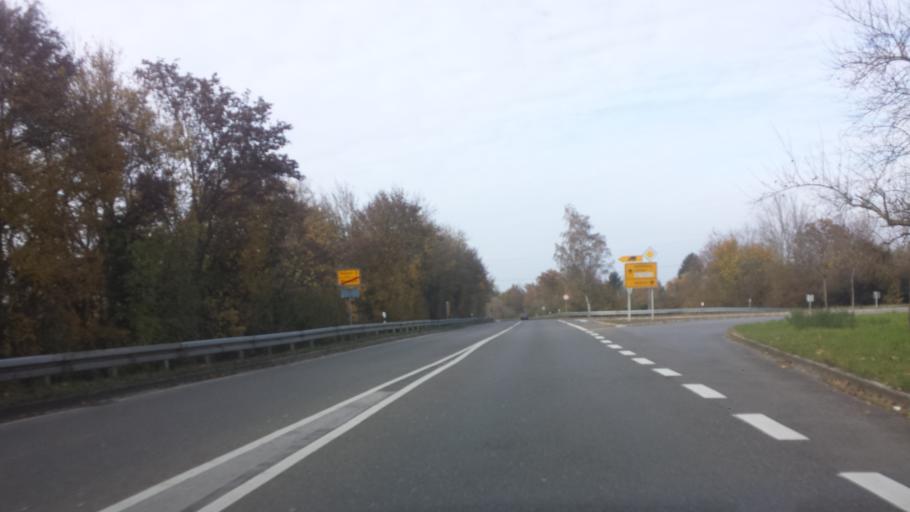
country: DE
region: Baden-Wuerttemberg
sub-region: Karlsruhe Region
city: Wiesloch
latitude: 49.3035
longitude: 8.6971
